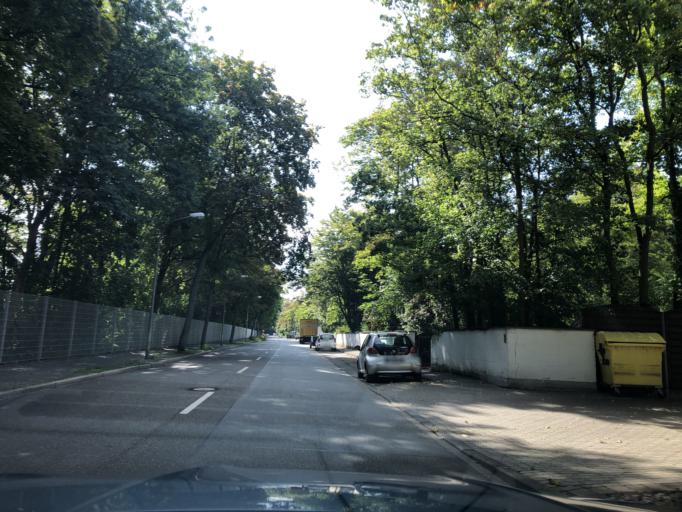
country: DE
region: Rheinland-Pfalz
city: Gartenstadt
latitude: 49.4924
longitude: 8.4079
